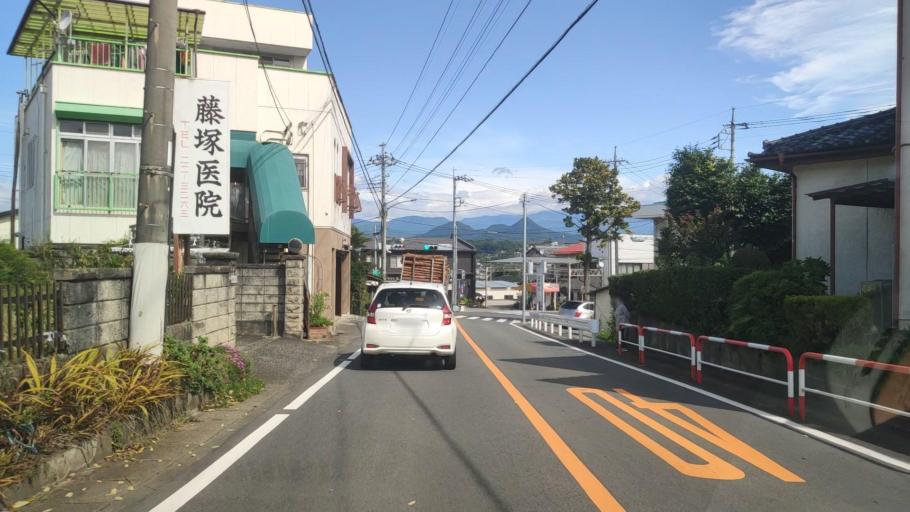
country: JP
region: Gunma
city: Numata
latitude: 36.6296
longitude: 139.0312
